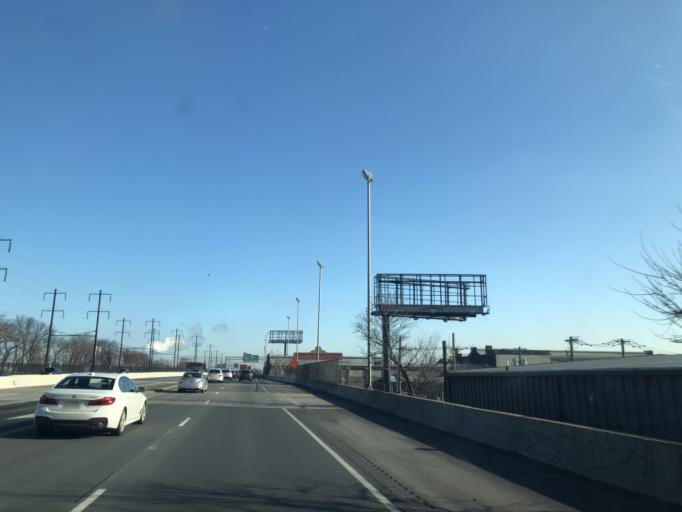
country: US
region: New Jersey
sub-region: Hudson County
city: Harrison
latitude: 40.7239
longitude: -74.1427
